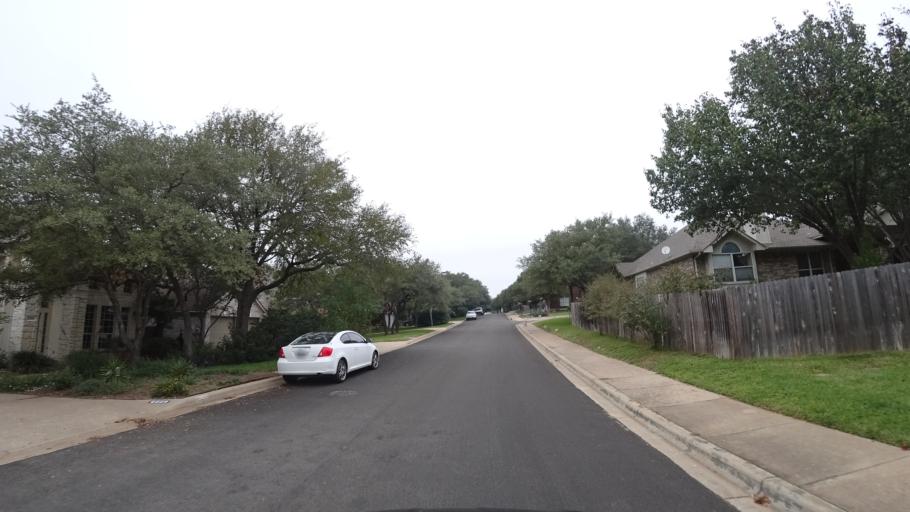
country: US
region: Texas
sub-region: Travis County
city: Shady Hollow
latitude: 30.1813
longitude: -97.8932
